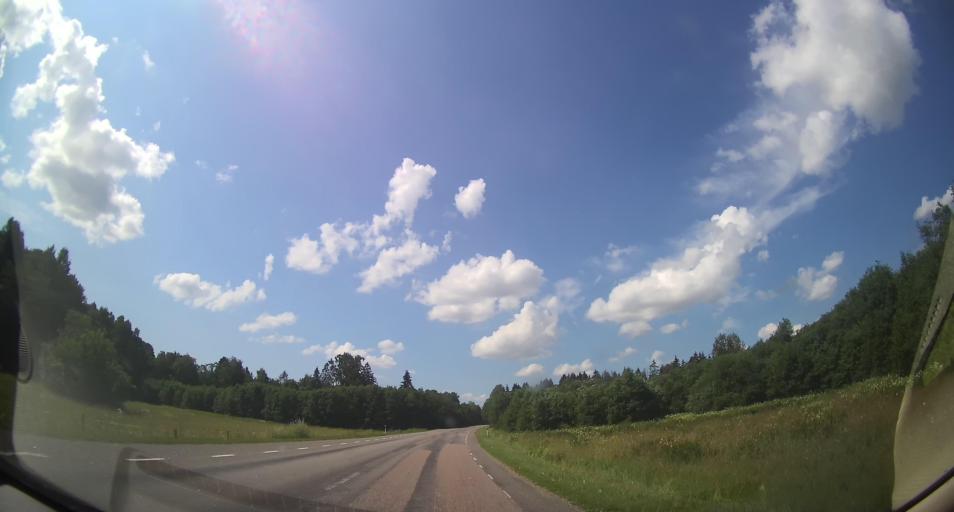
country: EE
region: Raplamaa
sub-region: Maerjamaa vald
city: Marjamaa
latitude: 58.8968
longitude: 24.2580
